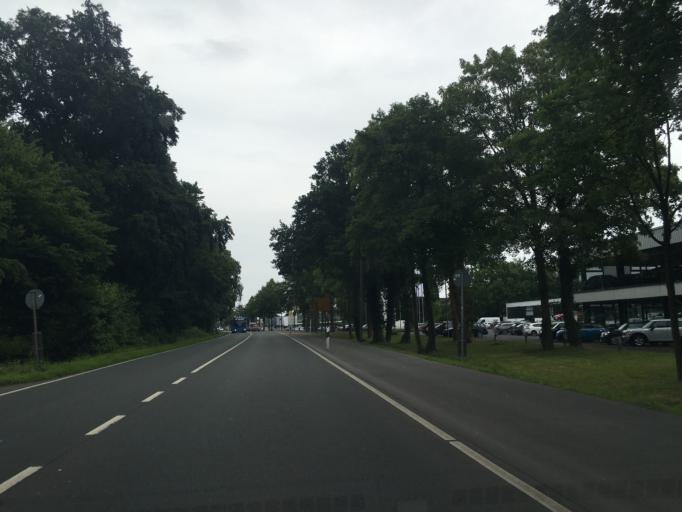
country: DE
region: North Rhine-Westphalia
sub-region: Regierungsbezirk Munster
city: Muenster
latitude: 51.9250
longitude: 7.5690
